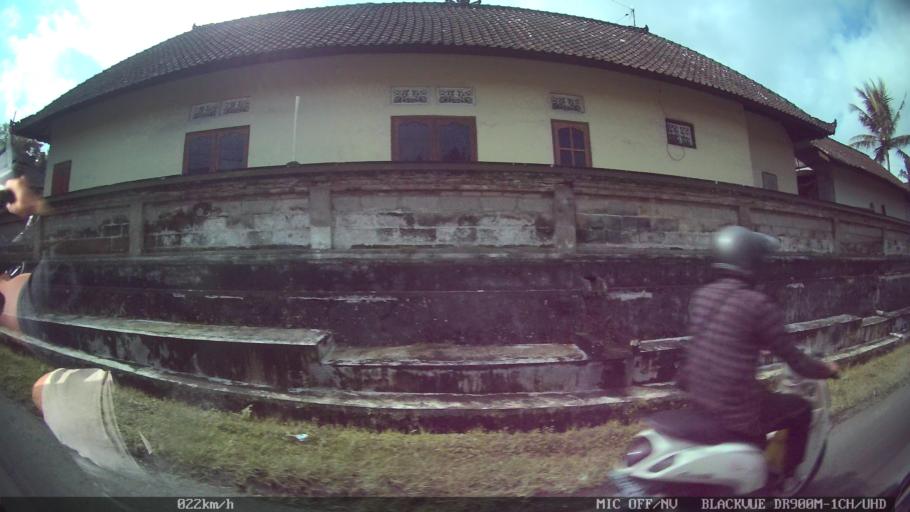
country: ID
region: Bali
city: Banjar Pesalakan
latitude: -8.5119
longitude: 115.3021
